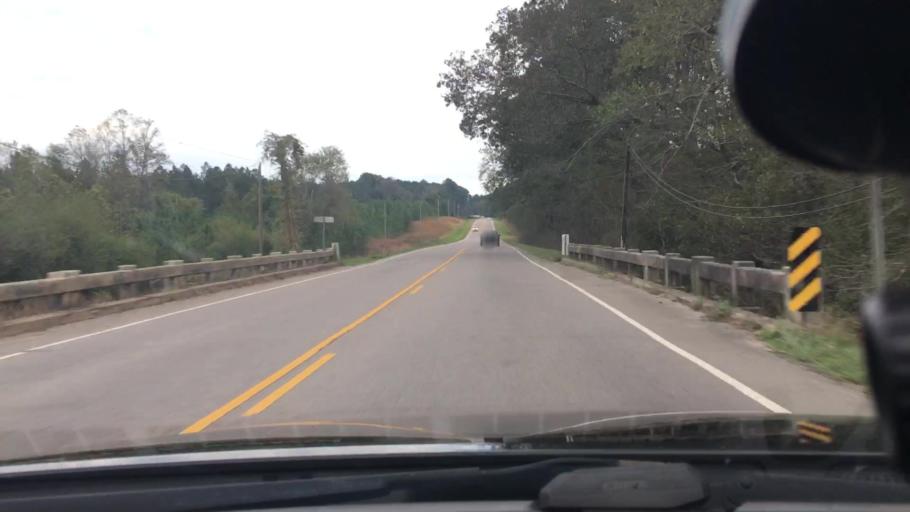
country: US
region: North Carolina
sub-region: Moore County
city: Carthage
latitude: 35.3830
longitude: -79.4855
